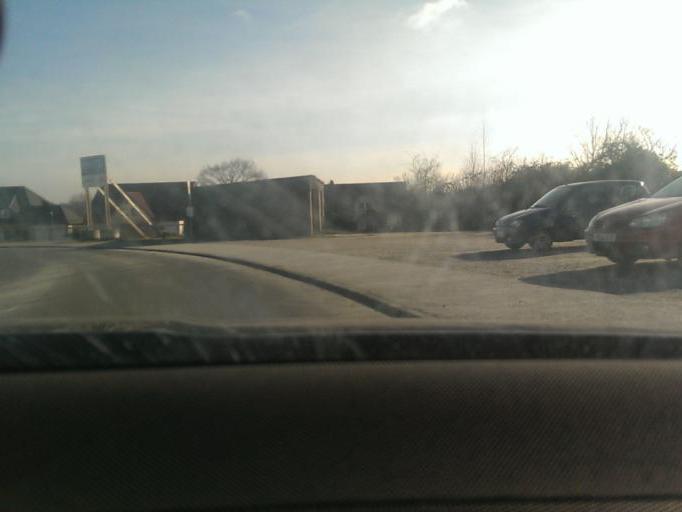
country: DE
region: North Rhine-Westphalia
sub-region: Regierungsbezirk Detmold
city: Delbruck
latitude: 51.7626
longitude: 8.5589
